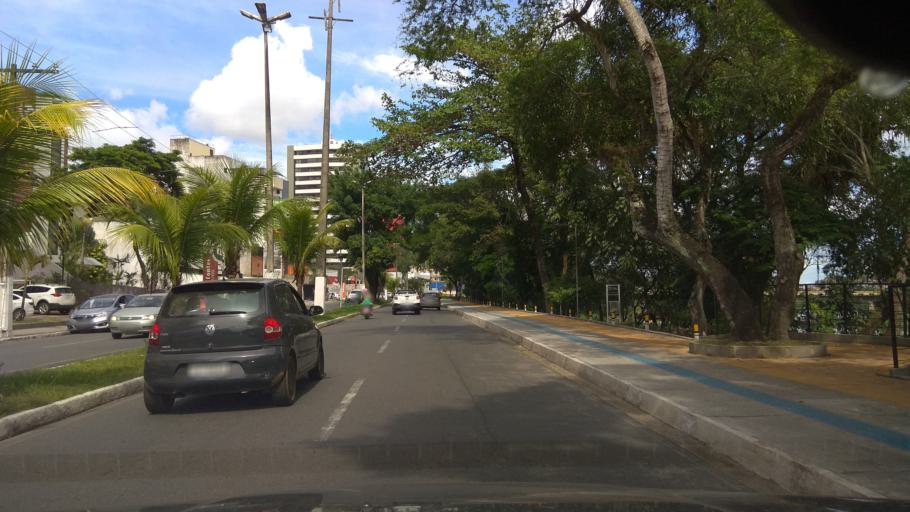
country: BR
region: Bahia
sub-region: Itabuna
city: Itabuna
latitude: -14.7974
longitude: -39.2752
